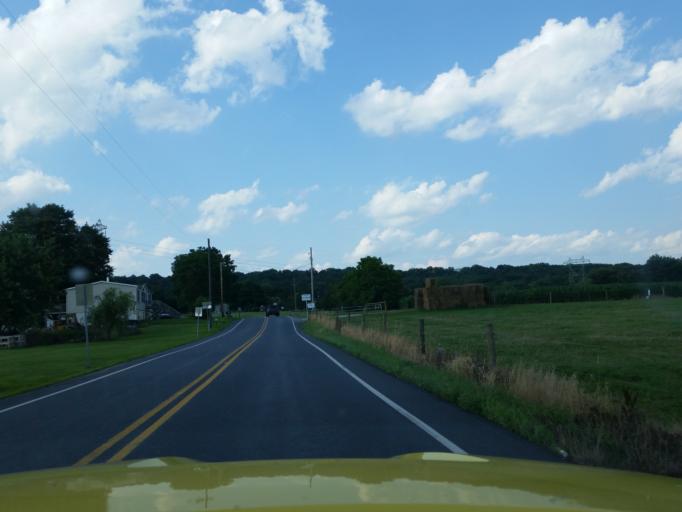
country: US
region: Pennsylvania
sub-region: Lebanon County
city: Campbelltown
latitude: 40.2158
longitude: -76.5051
